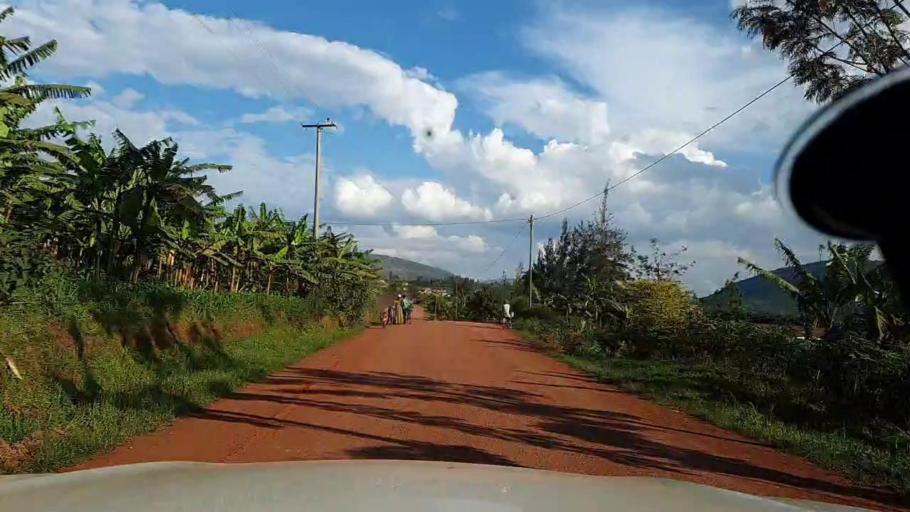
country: RW
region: Kigali
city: Kigali
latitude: -1.8916
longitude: 29.9578
